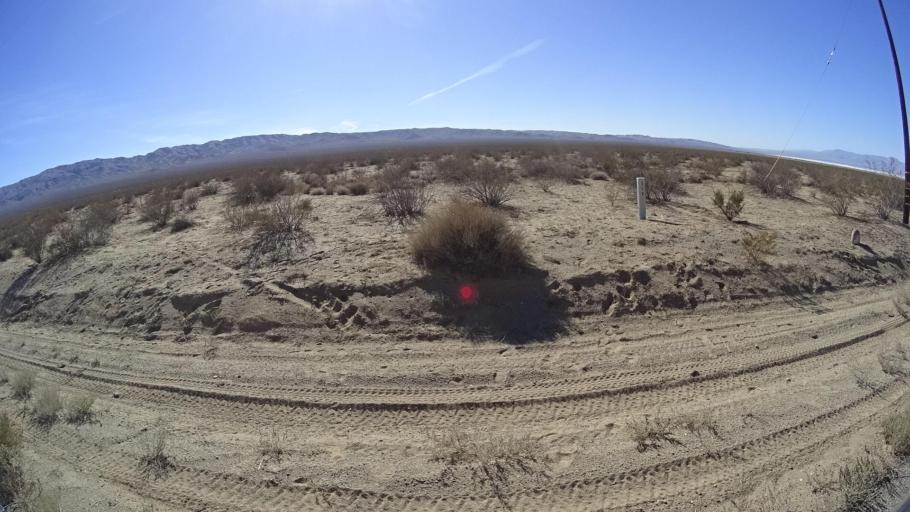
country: US
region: California
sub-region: Kern County
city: Ridgecrest
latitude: 35.3880
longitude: -117.7546
